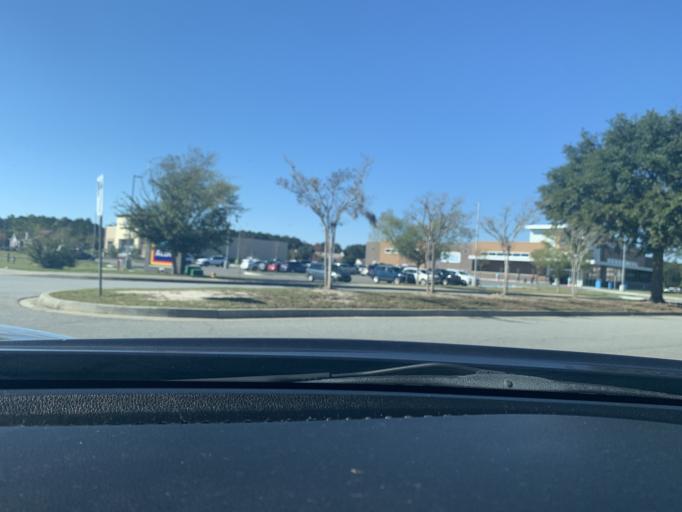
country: US
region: Georgia
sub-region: Chatham County
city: Pooler
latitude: 32.1408
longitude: -81.2517
